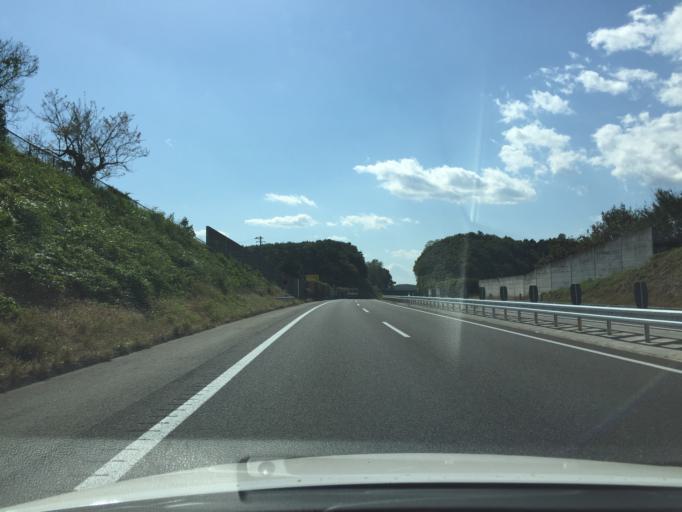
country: JP
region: Fukushima
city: Sukagawa
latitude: 37.2321
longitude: 140.3257
